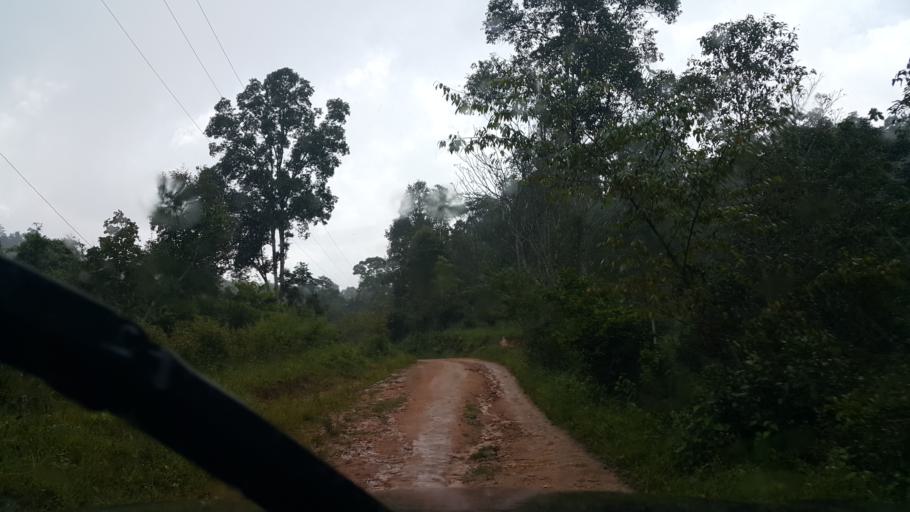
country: TH
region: Chiang Rai
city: Wiang Pa Pao
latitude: 19.1313
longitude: 99.3488
